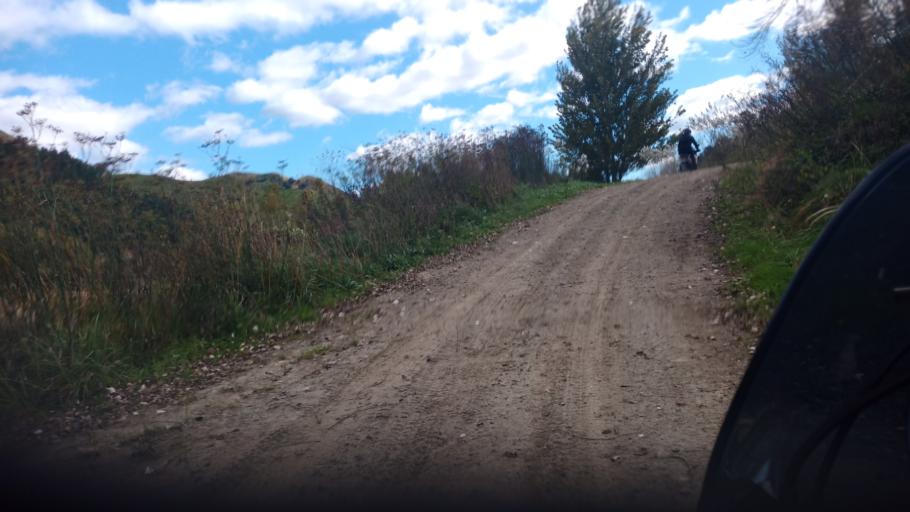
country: NZ
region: Gisborne
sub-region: Gisborne District
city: Gisborne
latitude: -38.4381
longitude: 177.7464
